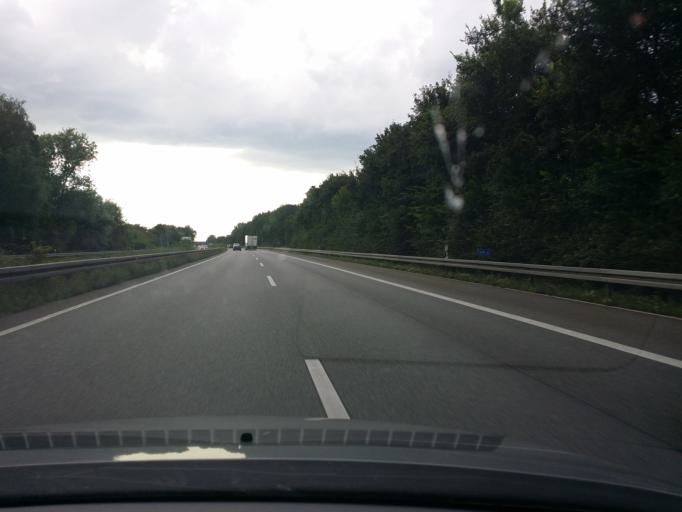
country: DE
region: Hesse
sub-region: Regierungsbezirk Darmstadt
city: Buttelborn
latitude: 49.8940
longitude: 8.5430
